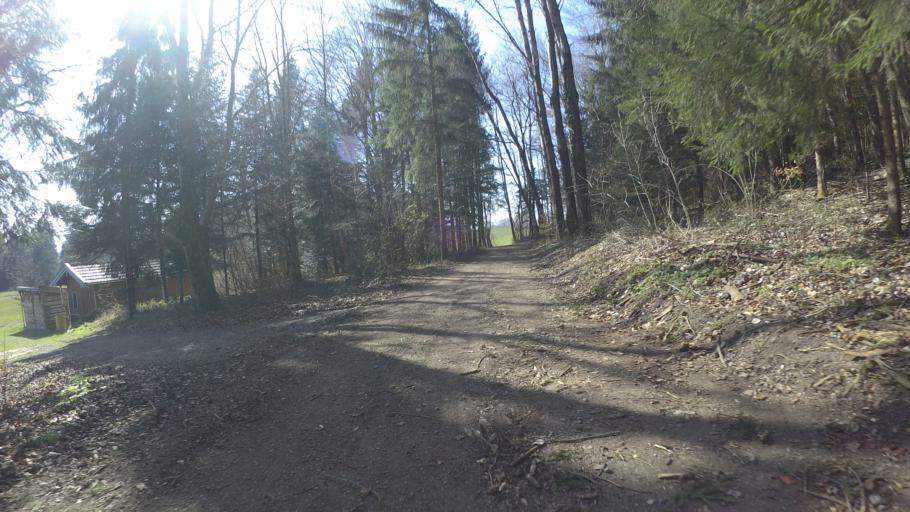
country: DE
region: Bavaria
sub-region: Upper Bavaria
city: Nussdorf
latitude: 47.9057
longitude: 12.5764
